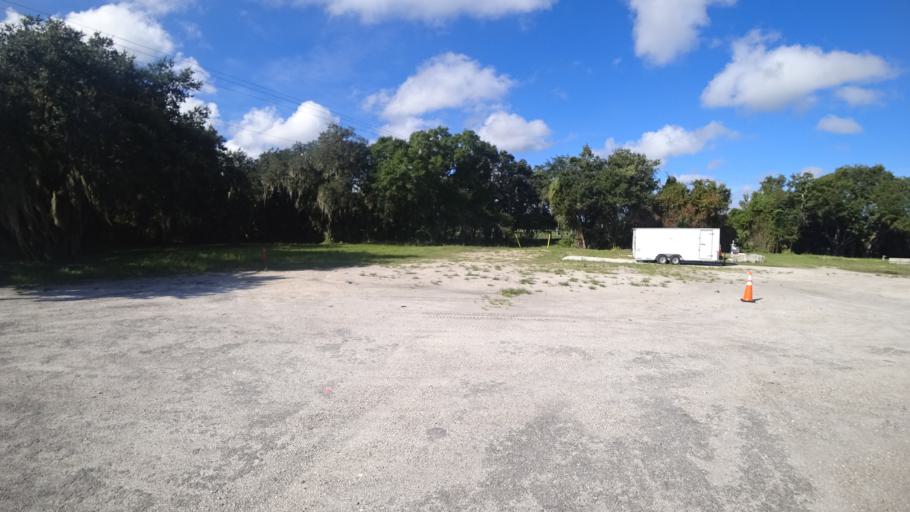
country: US
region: Florida
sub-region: Manatee County
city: Ellenton
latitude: 27.5843
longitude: -82.4786
